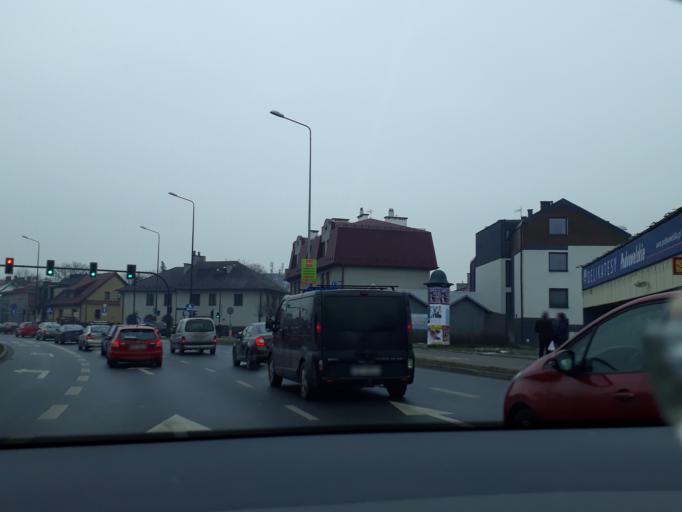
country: PL
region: Lesser Poland Voivodeship
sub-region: Krakow
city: Krakow
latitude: 50.0732
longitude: 19.9804
